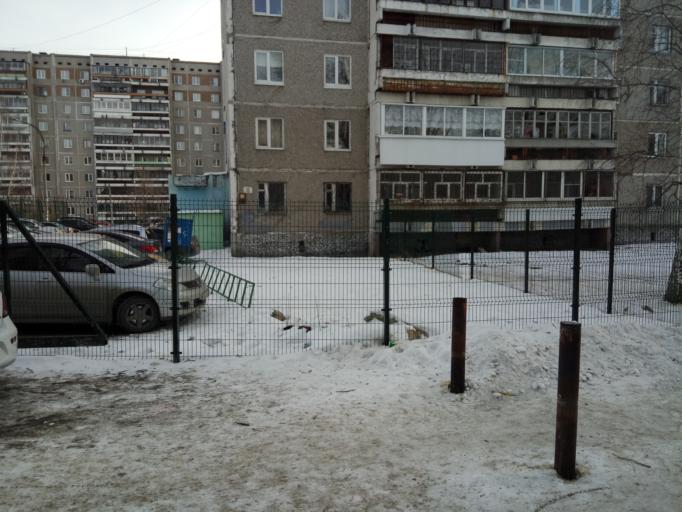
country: RU
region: Sverdlovsk
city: Yekaterinburg
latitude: 56.8371
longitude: 60.6749
